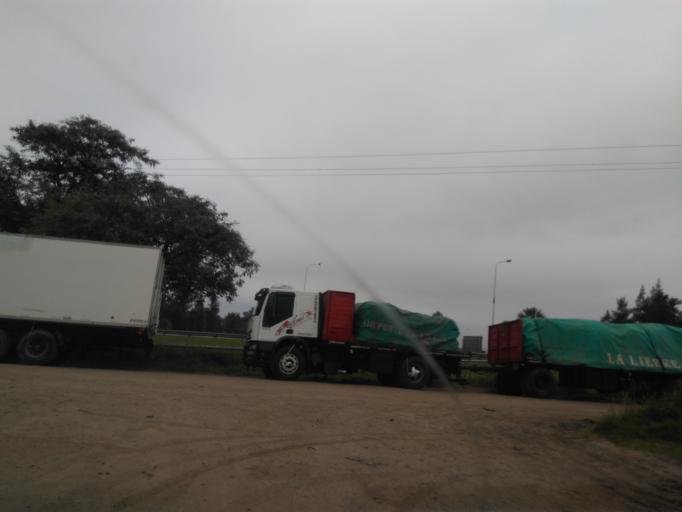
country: AR
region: Chaco
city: Fontana
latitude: -27.4460
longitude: -59.0251
